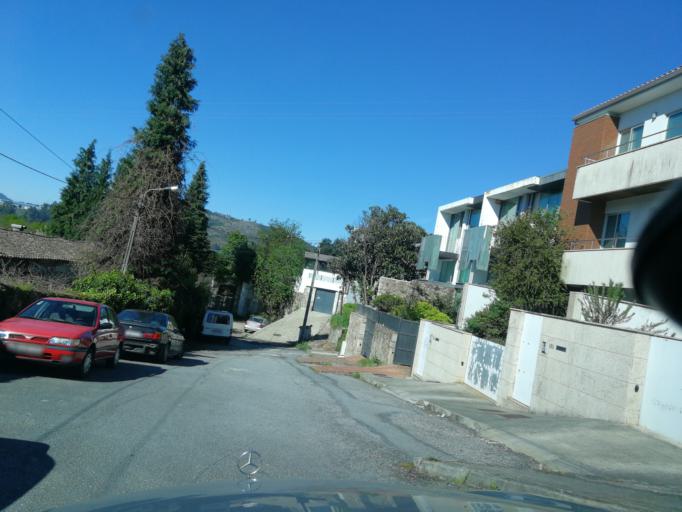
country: PT
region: Braga
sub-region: Braga
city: Braga
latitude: 41.5400
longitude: -8.4460
